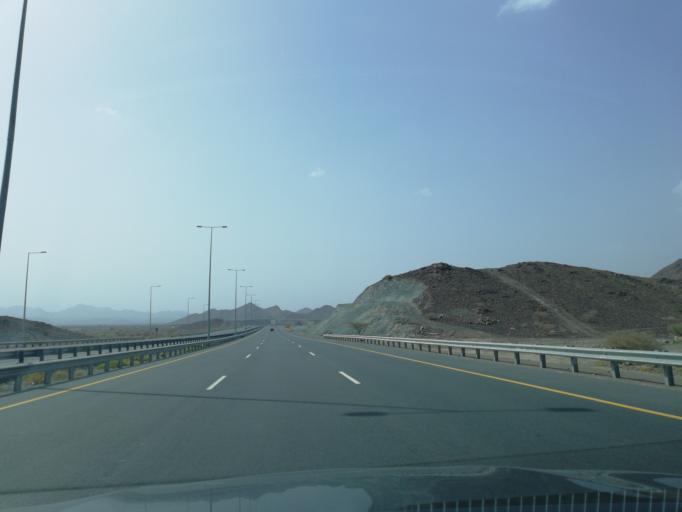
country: OM
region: Ash Sharqiyah
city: Ibra'
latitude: 22.9050
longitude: 58.2696
